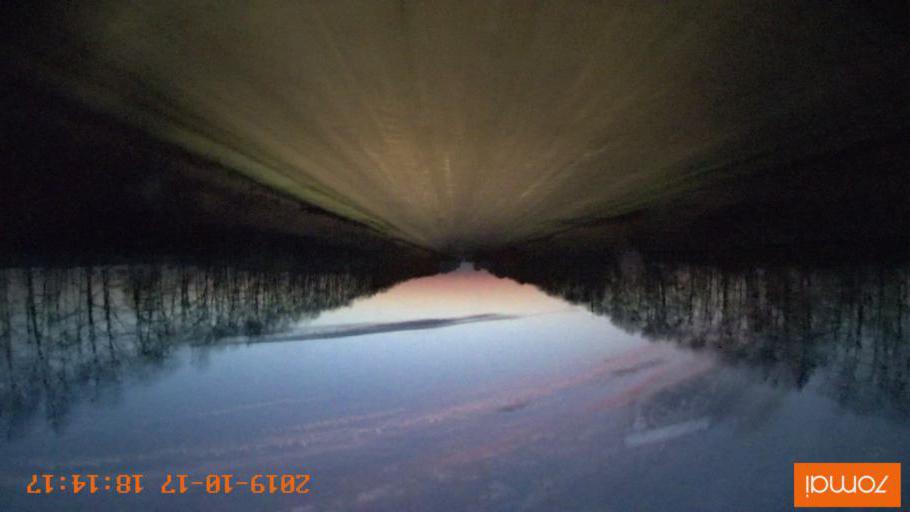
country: RU
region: Tula
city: Kurkino
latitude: 53.4077
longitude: 38.5663
